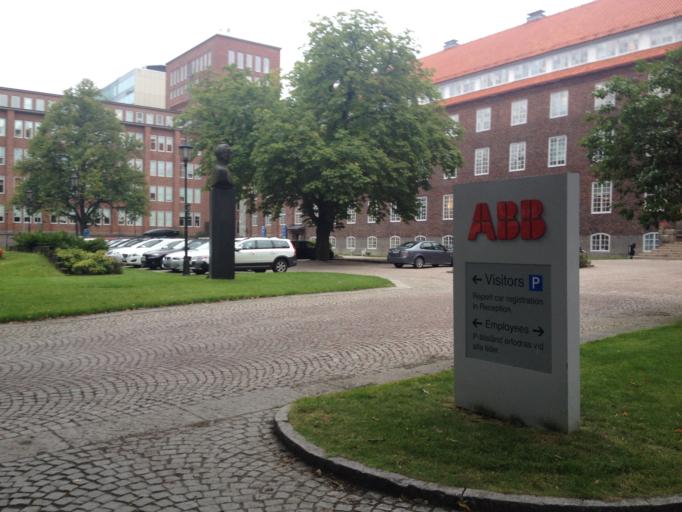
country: SE
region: Vaestmanland
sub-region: Vasteras
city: Vasteras
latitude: 59.6084
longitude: 16.5517
